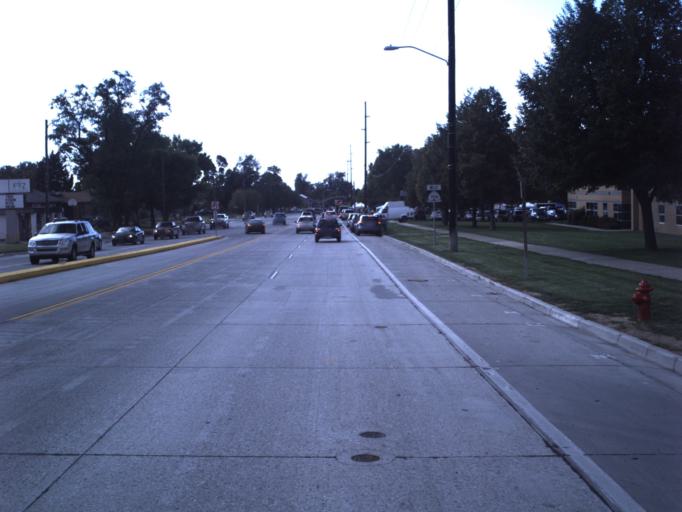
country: US
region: Utah
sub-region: Davis County
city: Bountiful
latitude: 40.8937
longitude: -111.8807
